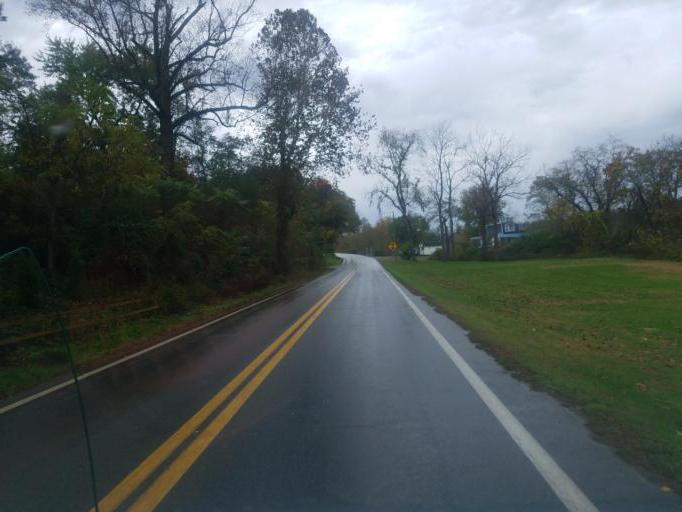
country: US
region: West Virginia
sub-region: Wood County
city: Williamstown
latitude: 39.4038
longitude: -81.4564
